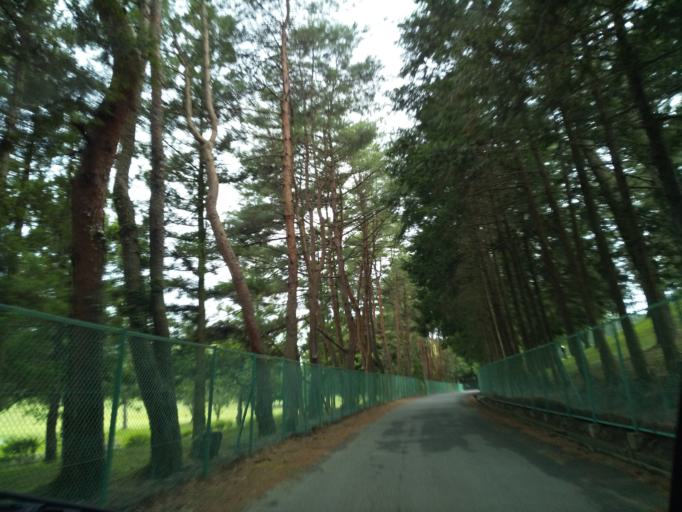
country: JP
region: Kanagawa
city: Atsugi
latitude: 35.4798
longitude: 139.3259
